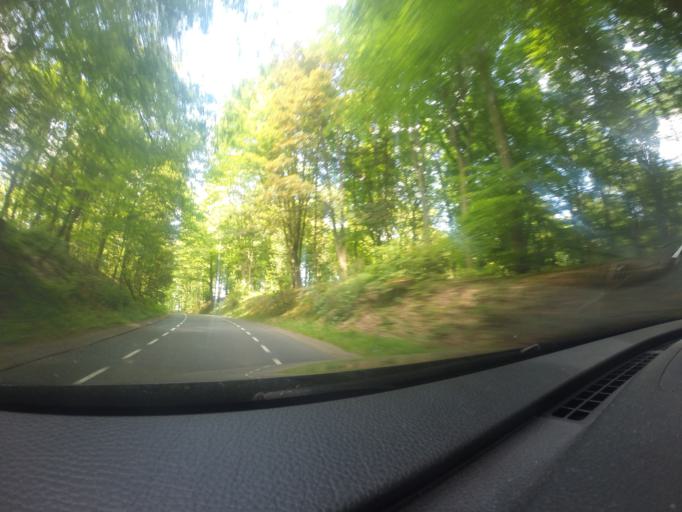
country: NL
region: Gelderland
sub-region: Gemeente Renkum
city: Heelsum
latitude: 51.9721
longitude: 5.7762
